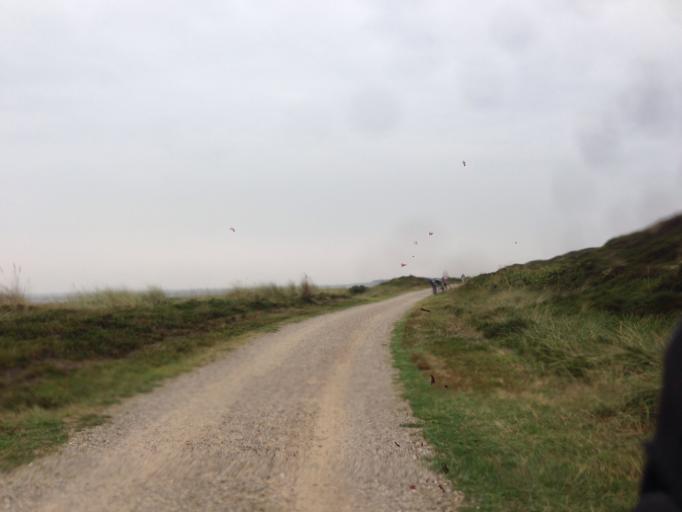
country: DE
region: Schleswig-Holstein
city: Westerland
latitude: 54.8365
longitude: 8.2957
